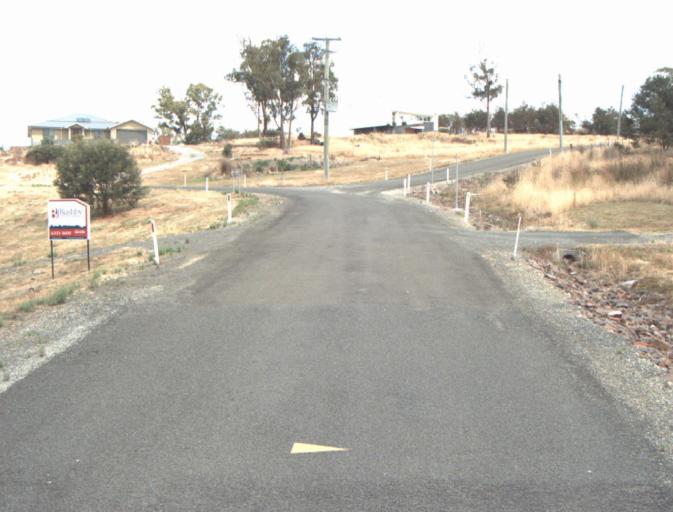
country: AU
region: Tasmania
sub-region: Launceston
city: Mayfield
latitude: -41.3022
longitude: 147.0418
